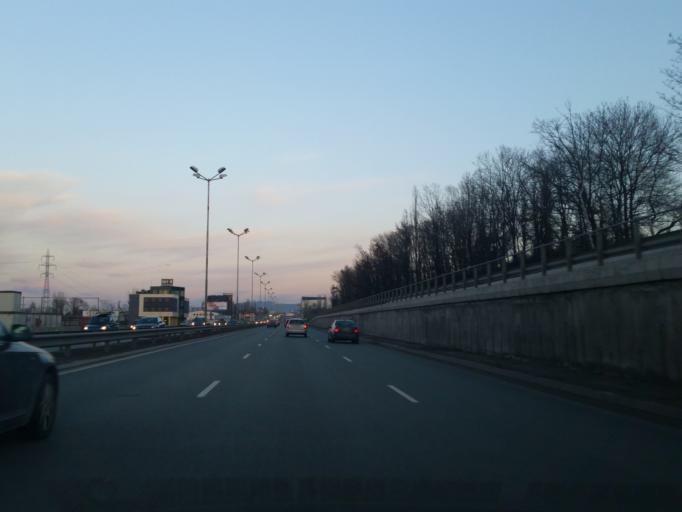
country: BG
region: Sofia-Capital
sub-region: Stolichna Obshtina
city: Sofia
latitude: 42.6474
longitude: 23.2983
